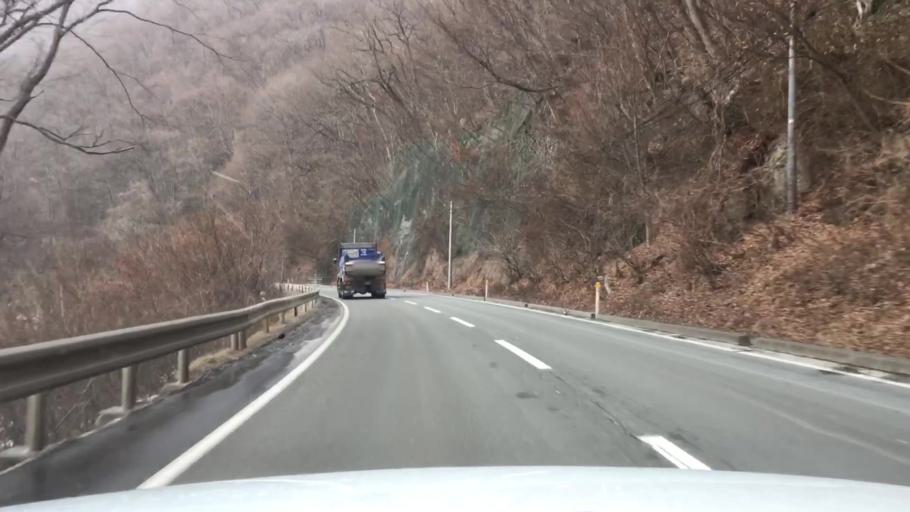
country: JP
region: Iwate
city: Tono
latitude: 39.6187
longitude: 141.4960
